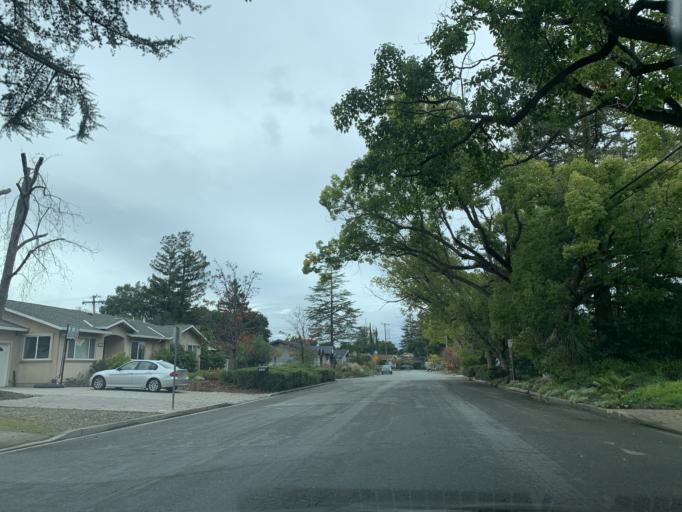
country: US
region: California
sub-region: Santa Clara County
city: Cupertino
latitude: 37.3296
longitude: -122.0584
